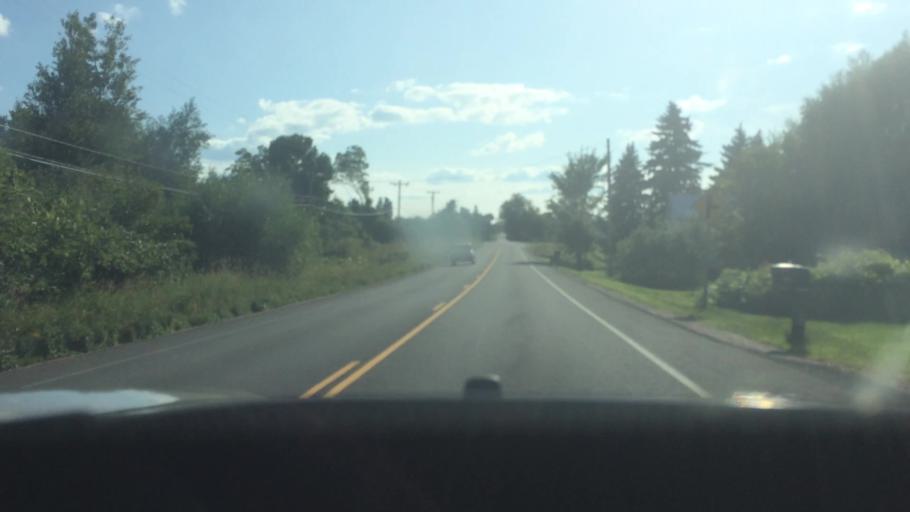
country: US
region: New York
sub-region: Franklin County
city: Malone
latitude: 44.7751
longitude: -74.5078
